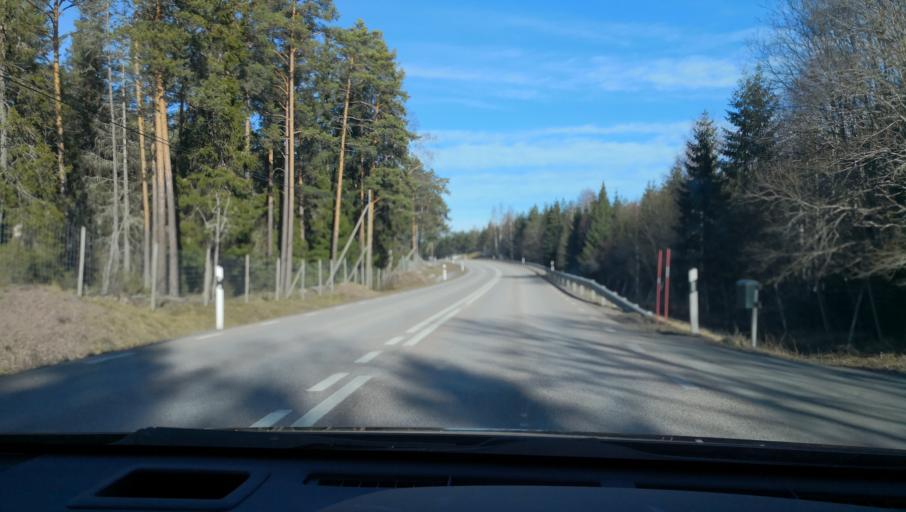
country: SE
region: Uppsala
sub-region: Uppsala Kommun
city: Vattholma
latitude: 60.1027
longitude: 17.7753
